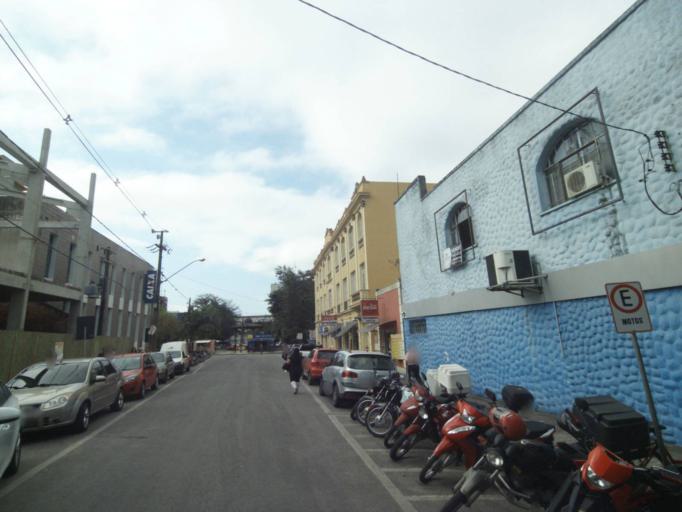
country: BR
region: Parana
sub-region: Paranagua
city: Paranagua
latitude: -25.5186
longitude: -48.5062
